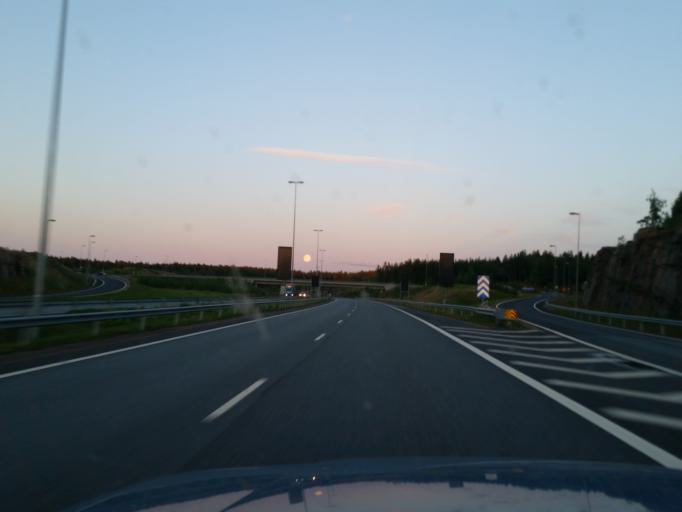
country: FI
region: Uusimaa
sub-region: Helsinki
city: Saukkola
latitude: 60.3447
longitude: 23.9070
